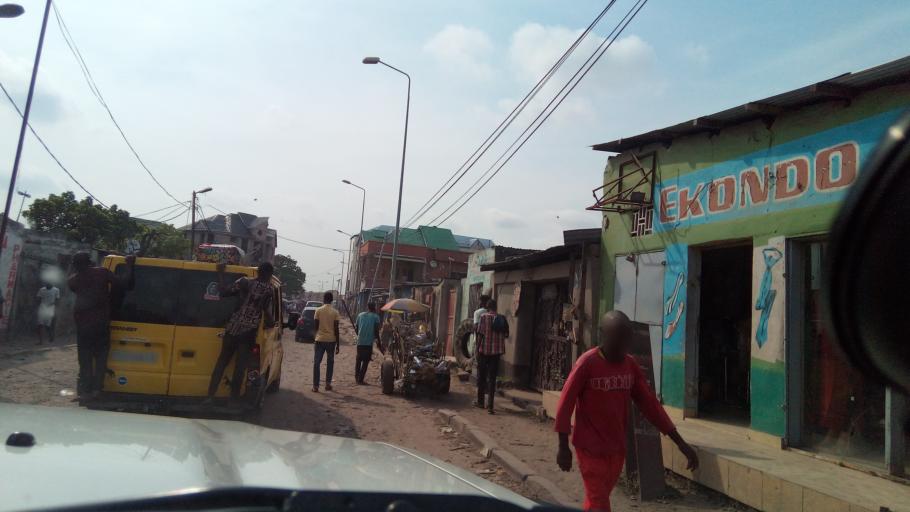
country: CD
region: Kinshasa
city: Kinshasa
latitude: -4.3502
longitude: 15.3224
